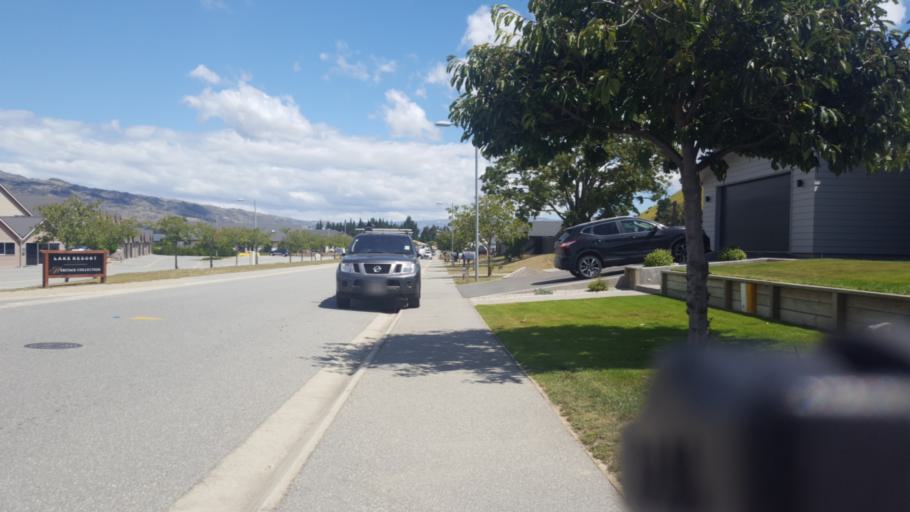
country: NZ
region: Otago
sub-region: Queenstown-Lakes District
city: Wanaka
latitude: -44.9793
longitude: 169.2358
